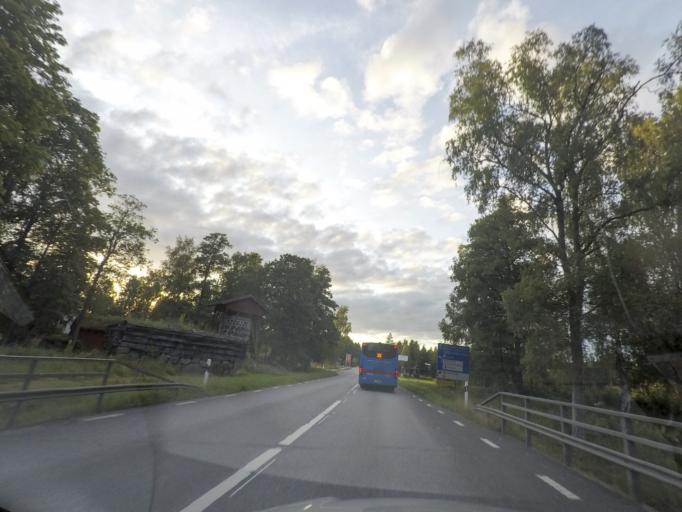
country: SE
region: OErebro
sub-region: Hallefors Kommun
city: Haellefors
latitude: 59.7047
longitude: 14.5465
